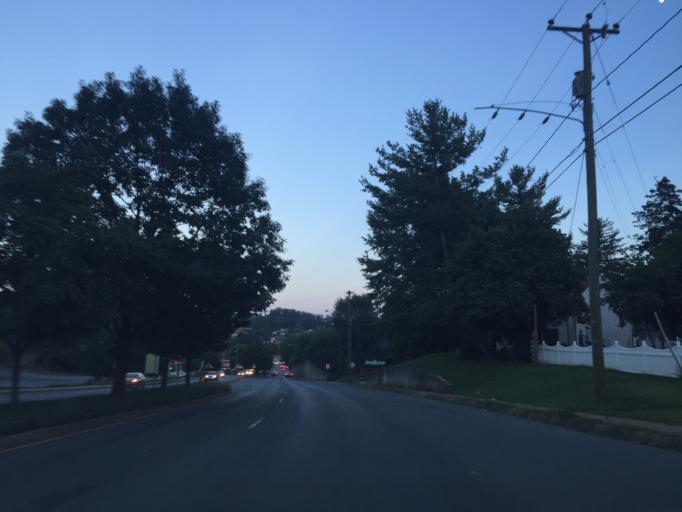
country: US
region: Virginia
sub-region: City of Charlottesville
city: Charlottesville
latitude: 38.0368
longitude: -78.4639
